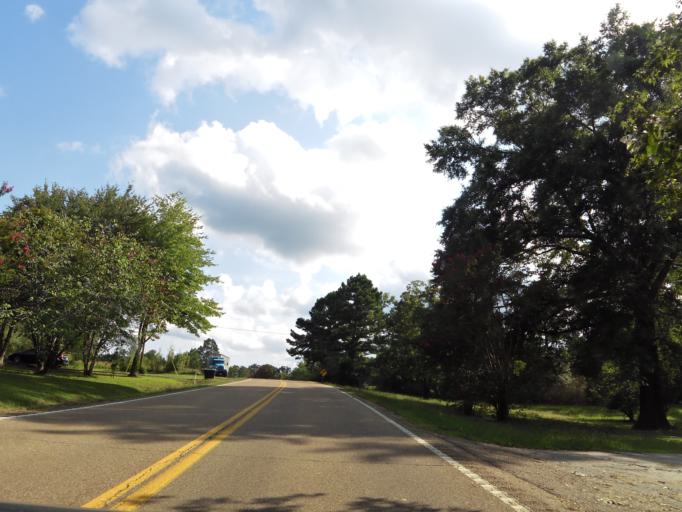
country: US
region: Mississippi
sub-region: Alcorn County
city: Farmington
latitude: 35.0661
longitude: -88.3943
